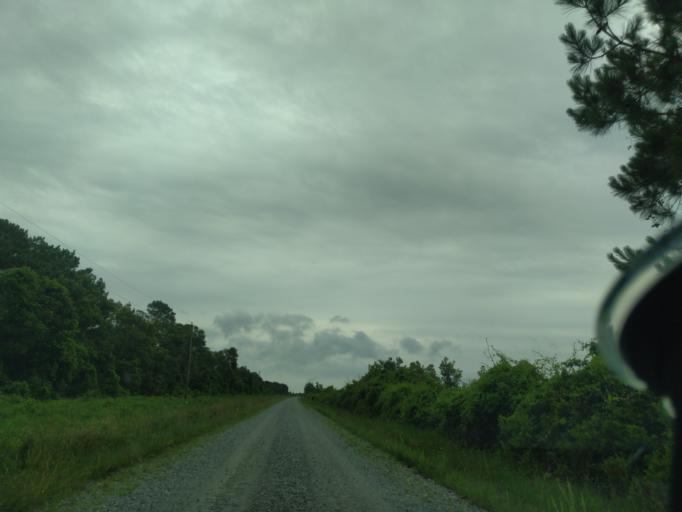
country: US
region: North Carolina
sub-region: Beaufort County
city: Belhaven
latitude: 35.7402
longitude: -76.4757
